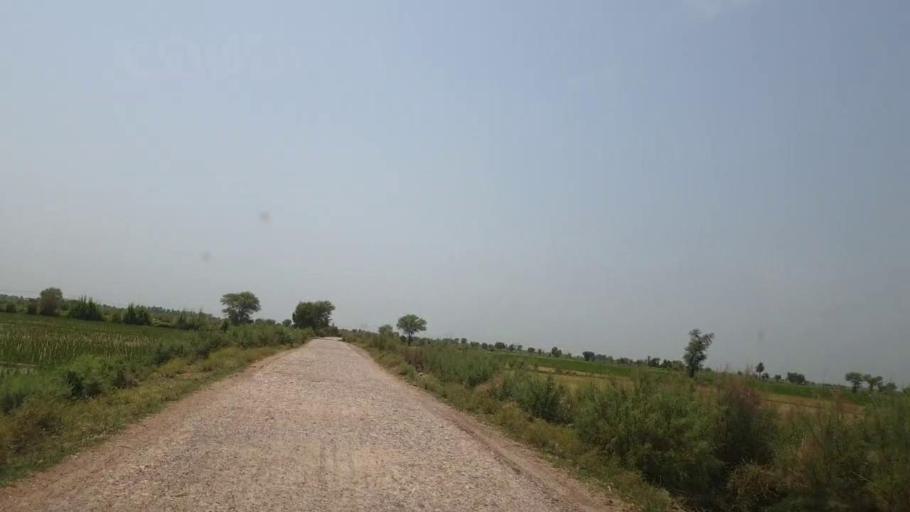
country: PK
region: Sindh
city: Shikarpur
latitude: 27.9038
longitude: 68.6330
